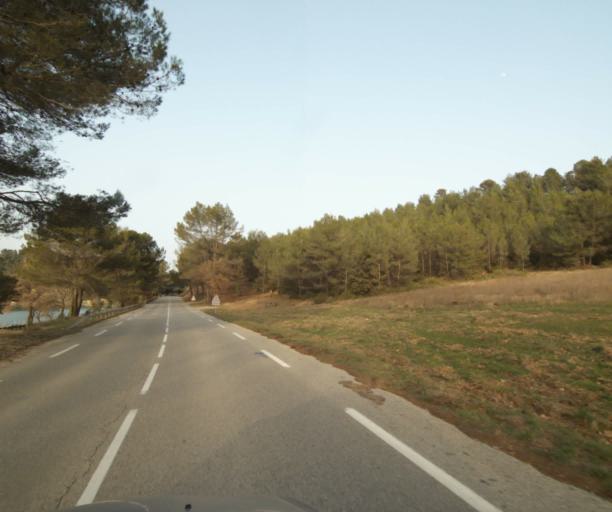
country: FR
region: Provence-Alpes-Cote d'Azur
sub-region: Departement du Vaucluse
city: Cadenet
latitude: 43.7036
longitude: 5.3504
